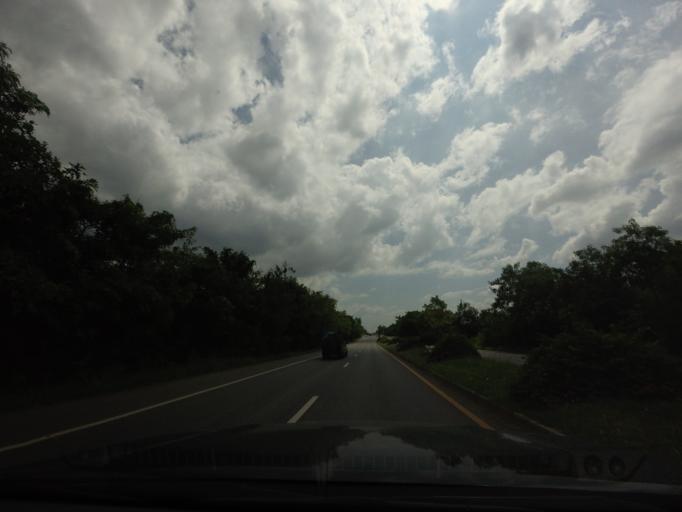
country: TH
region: Phetchabun
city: Phetchabun
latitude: 16.2160
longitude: 101.0890
